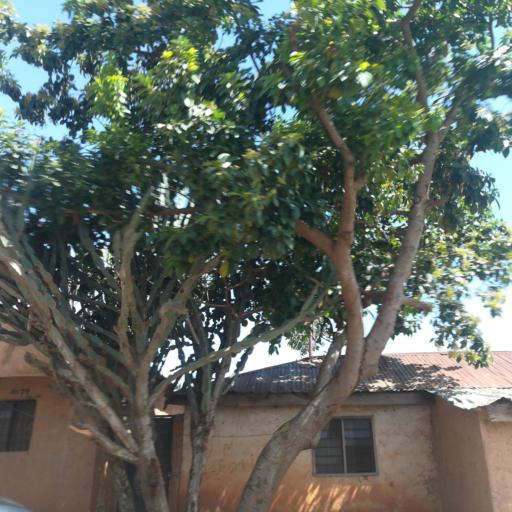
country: NG
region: Plateau
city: Bukuru
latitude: 9.7606
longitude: 8.8601
